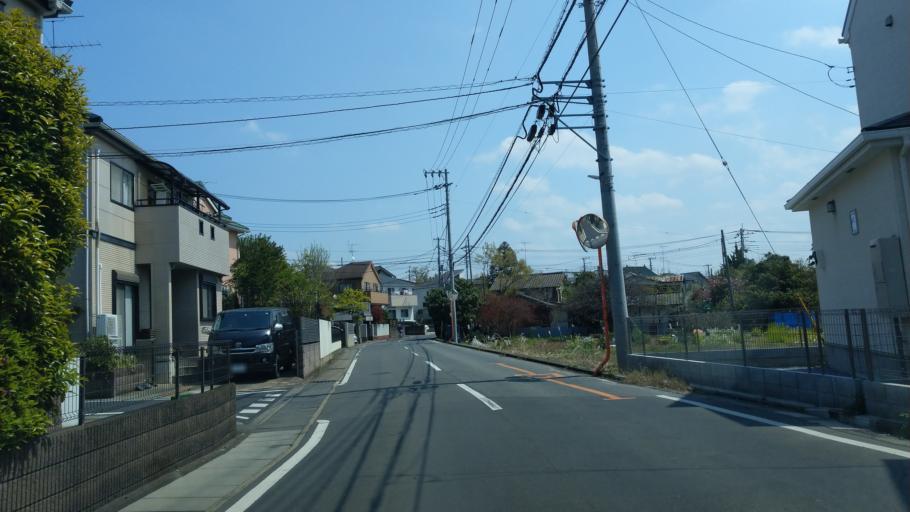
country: JP
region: Saitama
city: Saitama
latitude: 35.8992
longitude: 139.6534
